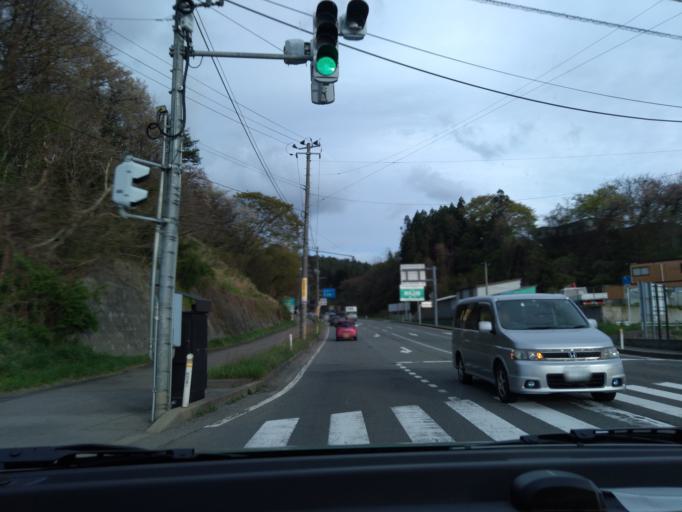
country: JP
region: Akita
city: Akita
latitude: 39.7462
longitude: 140.1319
